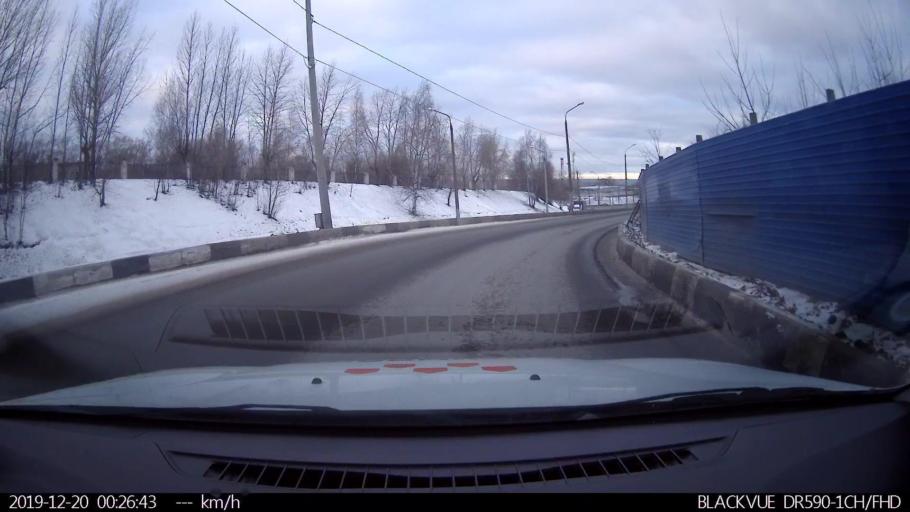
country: RU
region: Vladimir
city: Yur'yev-Pol'skiy
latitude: 56.6071
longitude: 39.5605
